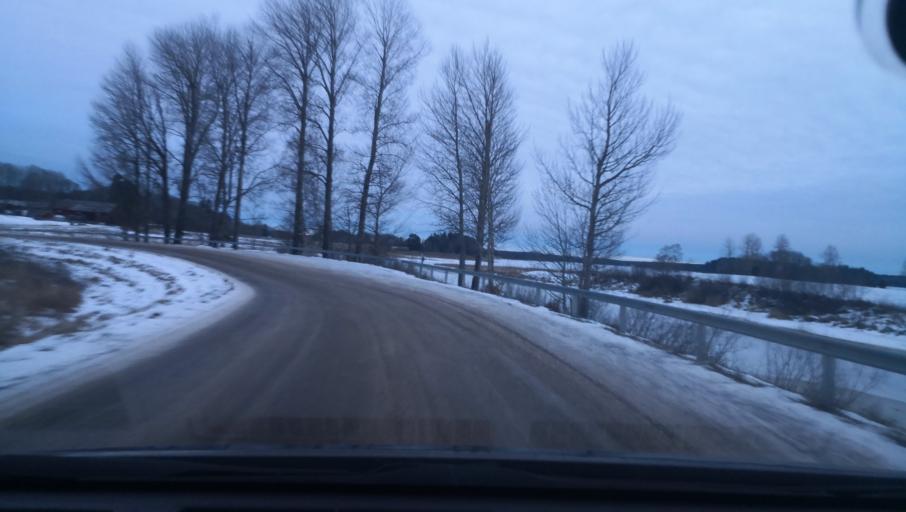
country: SE
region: Dalarna
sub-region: Avesta Kommun
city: Horndal
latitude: 60.1996
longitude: 16.4914
